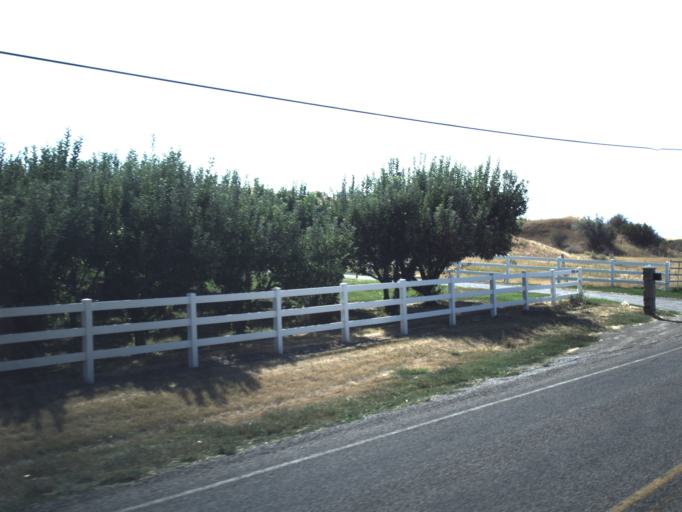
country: US
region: Utah
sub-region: Cache County
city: Hyrum
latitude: 41.5901
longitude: -111.8374
